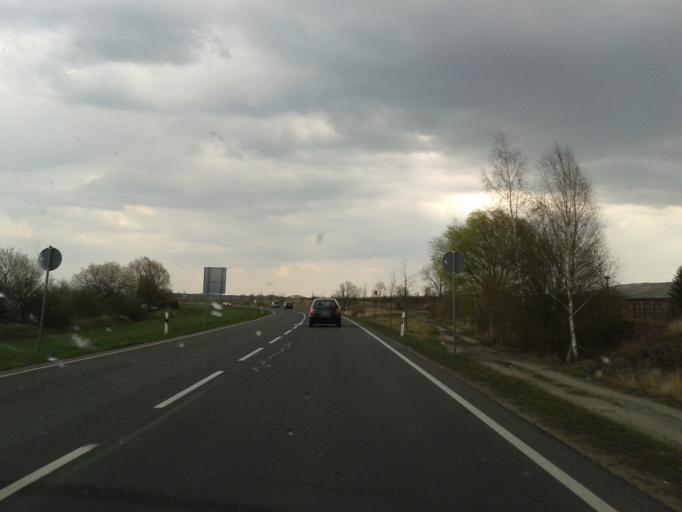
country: DE
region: Saxony-Anhalt
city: Salzwedel
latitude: 52.8583
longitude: 11.1673
